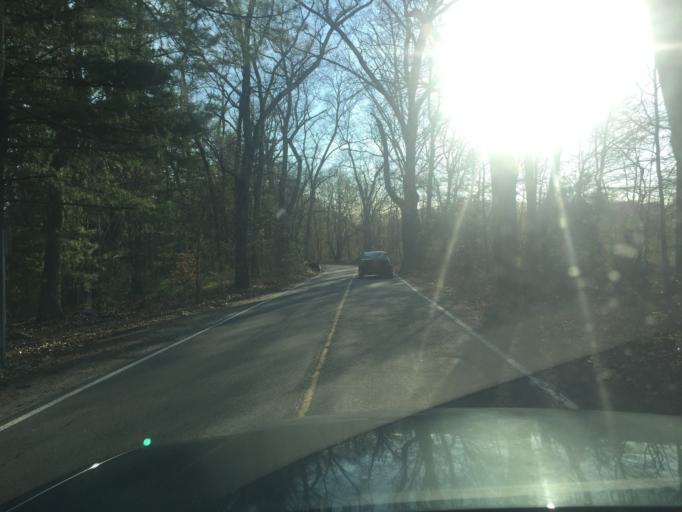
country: US
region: Massachusetts
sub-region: Middlesex County
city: Sherborn
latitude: 42.2272
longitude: -71.3495
